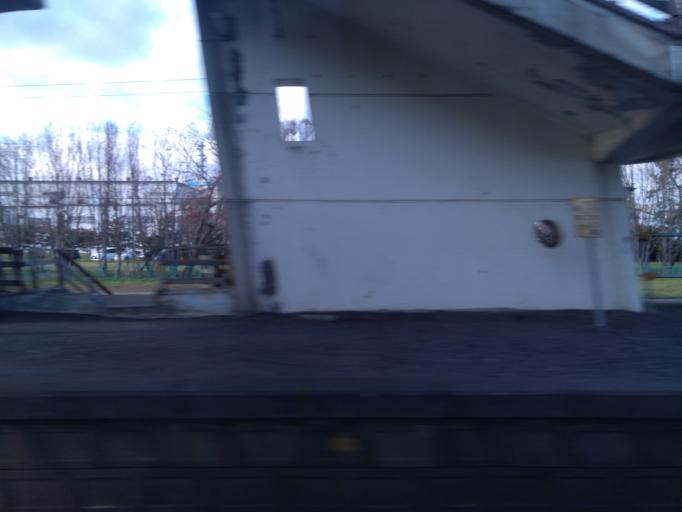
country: JP
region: Hokkaido
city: Shiraoi
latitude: 42.5091
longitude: 141.2863
